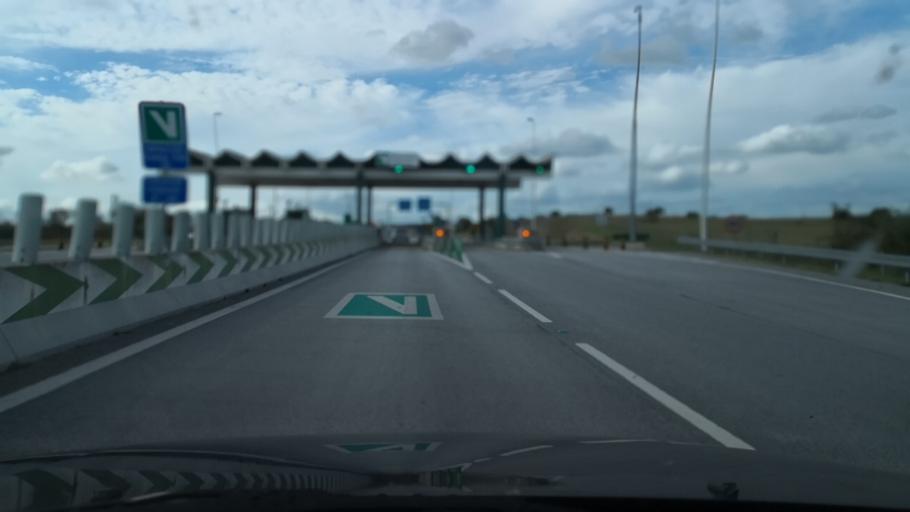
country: PT
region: Evora
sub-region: Evora
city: Evora
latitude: 38.6430
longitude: -7.8549
